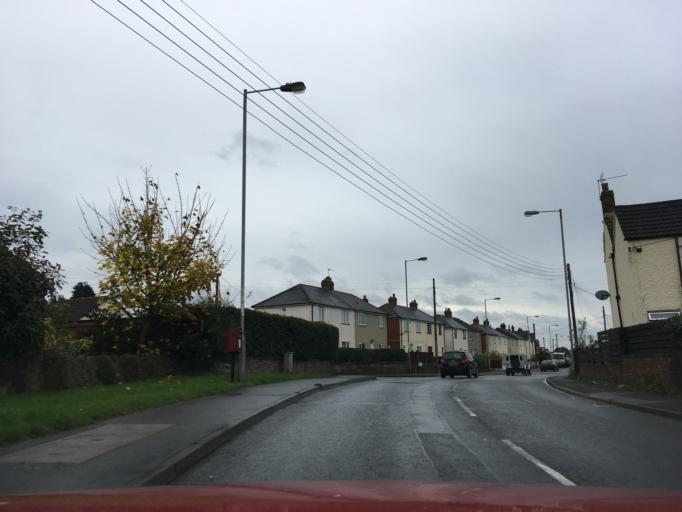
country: GB
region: Wales
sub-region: Monmouthshire
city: Caldicot
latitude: 51.5911
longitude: -2.7625
